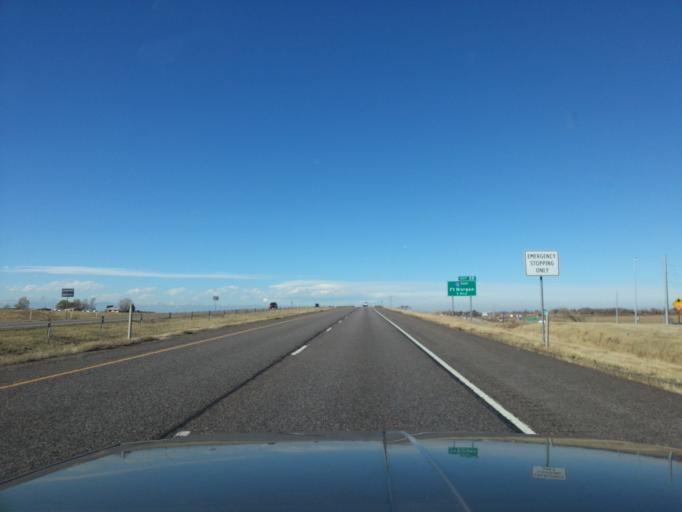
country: US
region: Colorado
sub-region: Adams County
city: Brighton
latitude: 39.9112
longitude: -104.7794
